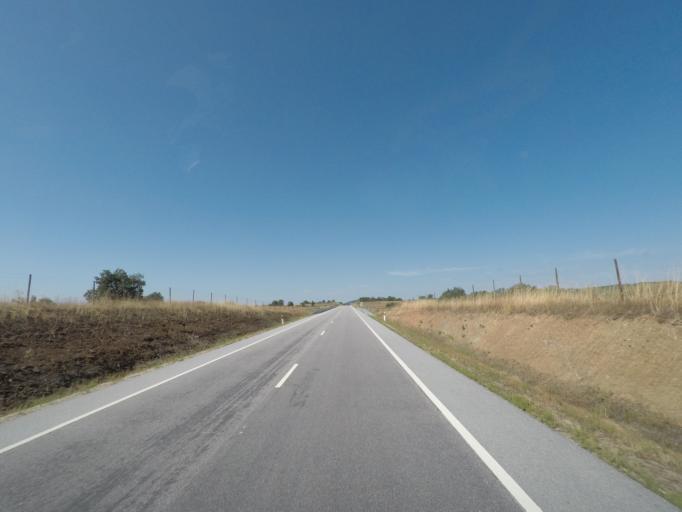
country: ES
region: Castille and Leon
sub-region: Provincia de Salamanca
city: Villarino de los Aires
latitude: 41.3612
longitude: -6.5412
